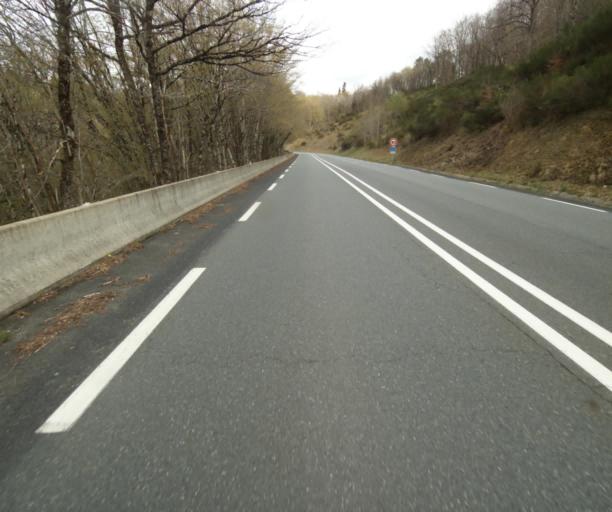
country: FR
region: Limousin
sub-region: Departement de la Correze
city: Sainte-Fortunade
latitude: 45.1902
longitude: 1.8430
